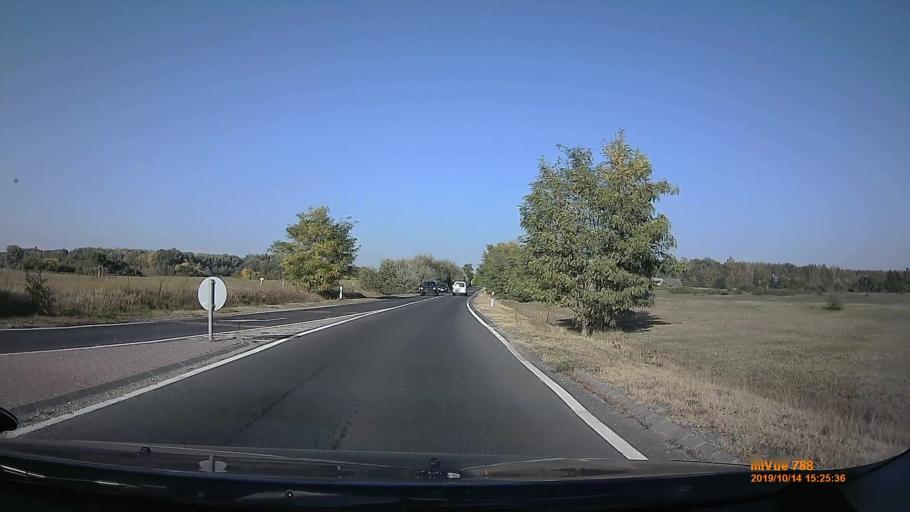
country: HU
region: Pest
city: Vecses
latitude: 47.4107
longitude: 19.3113
